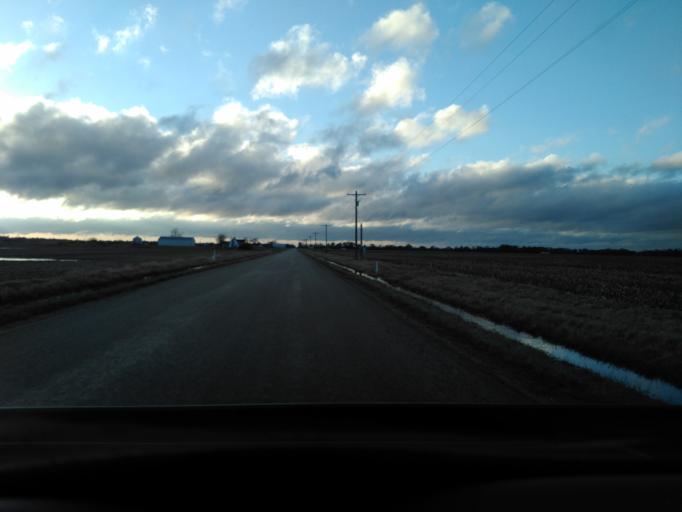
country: US
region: Illinois
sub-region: Effingham County
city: Altamont
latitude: 38.9576
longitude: -88.7320
